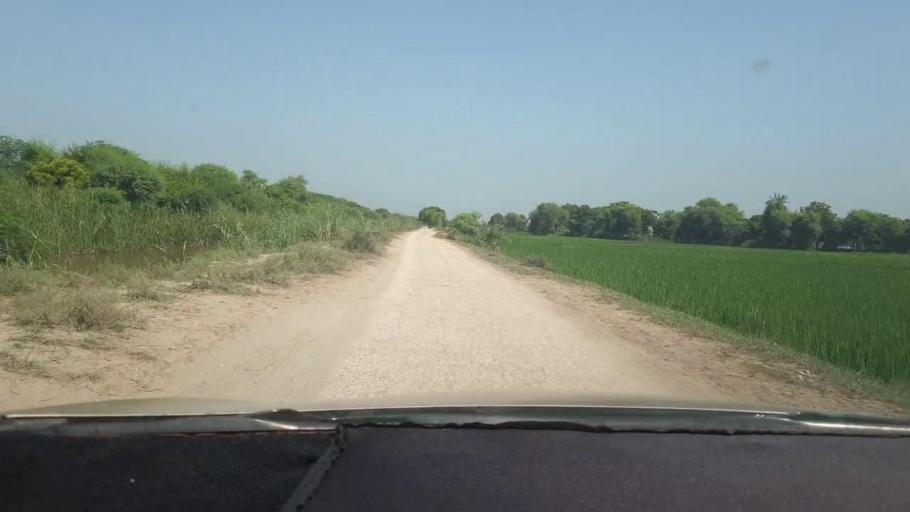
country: PK
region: Sindh
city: Miro Khan
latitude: 27.7036
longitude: 68.0832
